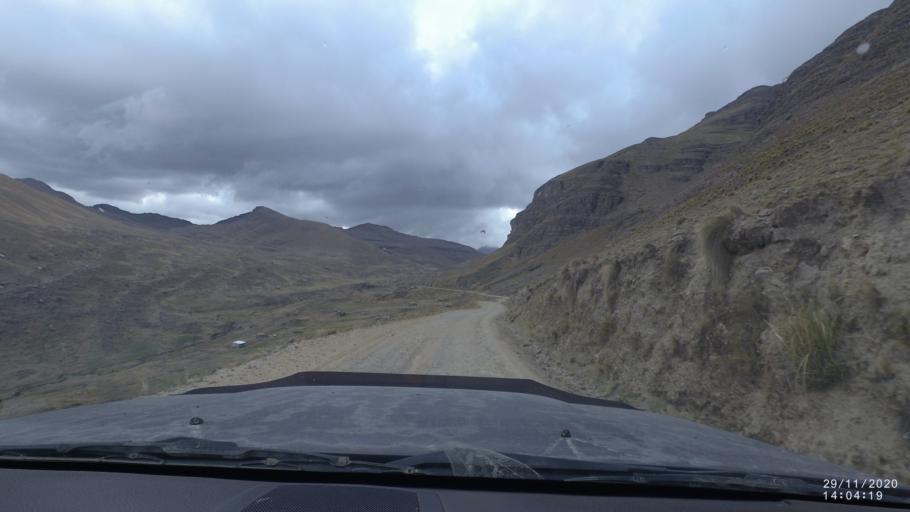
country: BO
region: Cochabamba
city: Sipe Sipe
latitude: -17.1999
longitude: -66.3764
